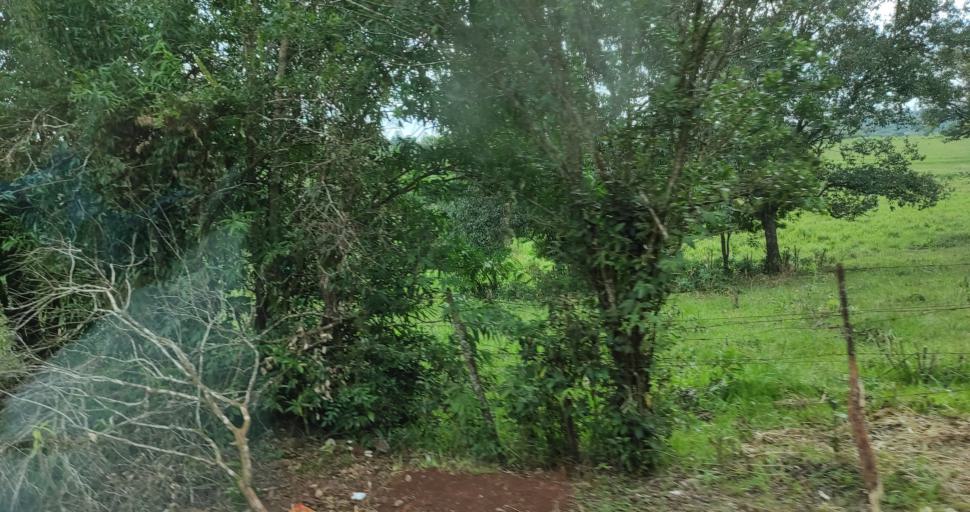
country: AR
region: Misiones
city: Puerto Libertad
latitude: -25.9631
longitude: -54.5942
